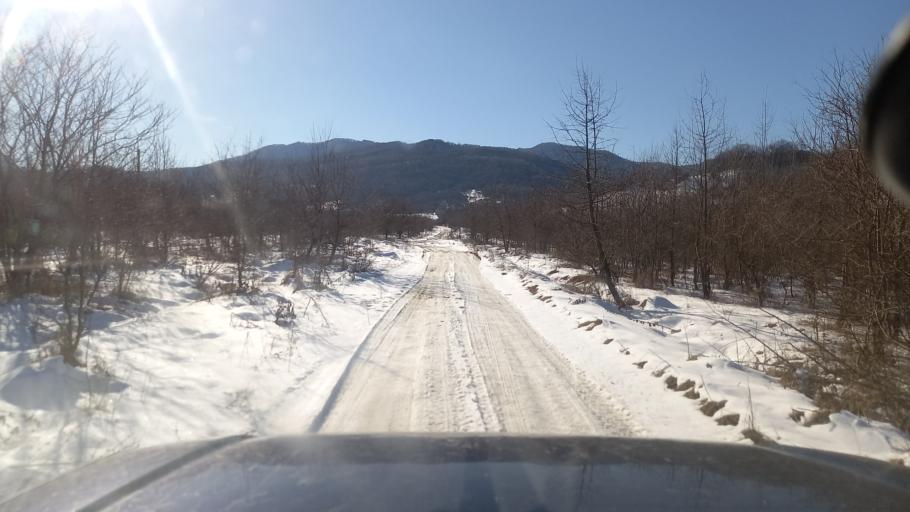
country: RU
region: Adygeya
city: Kamennomostskiy
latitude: 44.2084
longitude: 40.1603
